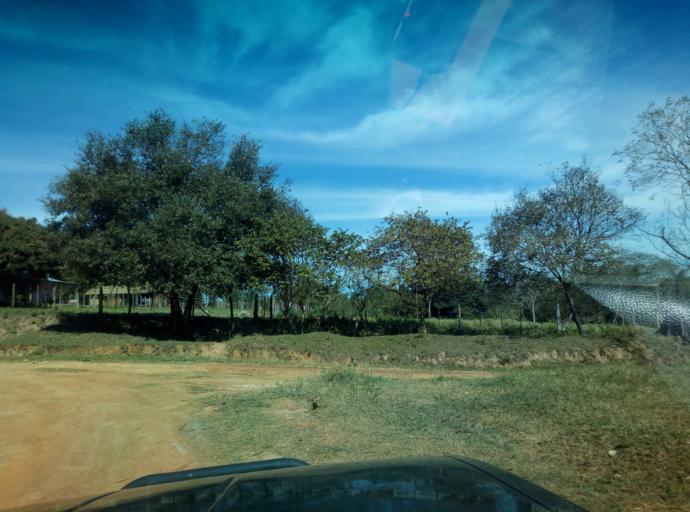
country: PY
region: Caaguazu
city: Carayao
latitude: -25.1896
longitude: -56.2551
